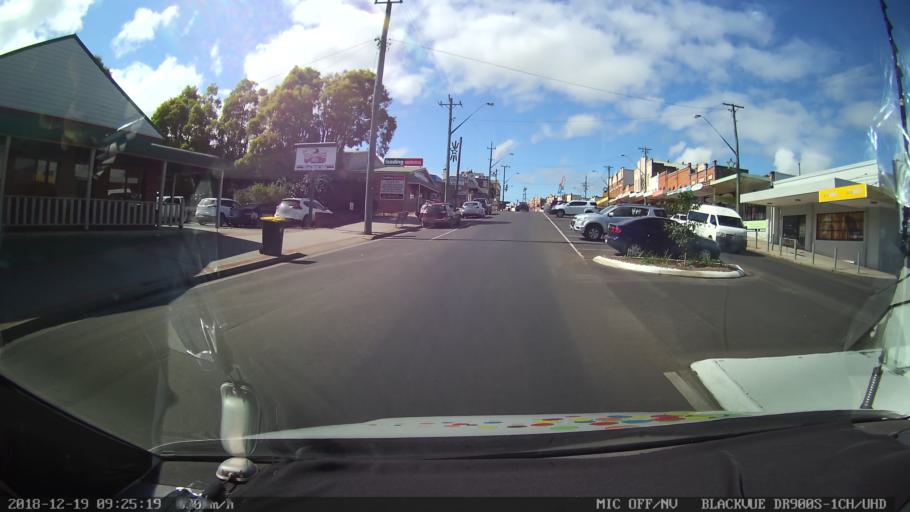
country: AU
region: New South Wales
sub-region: Kyogle
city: Kyogle
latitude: -28.6188
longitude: 153.0039
